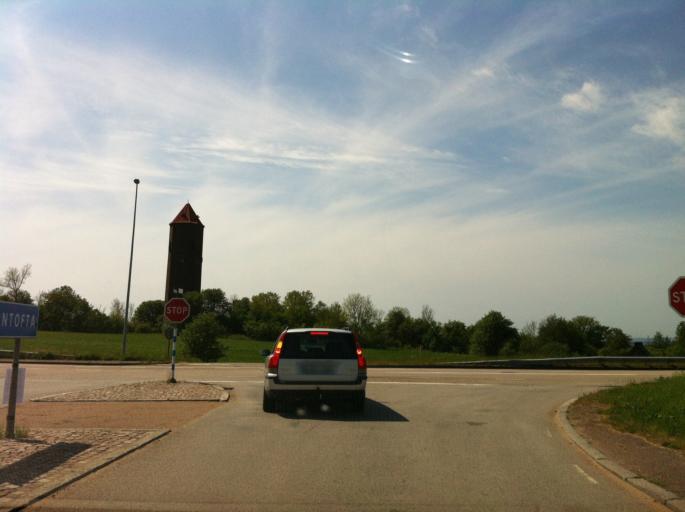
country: SE
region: Skane
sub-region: Helsingborg
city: Glumslov
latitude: 55.9308
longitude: 12.8430
